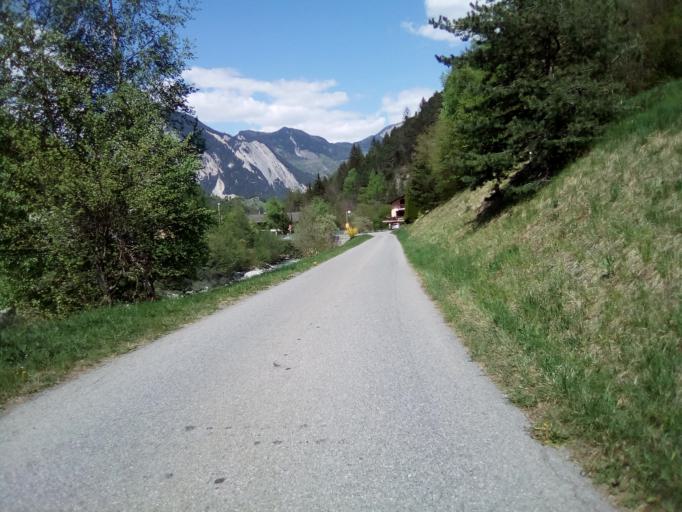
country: CH
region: Valais
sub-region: Entremont District
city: Orsieres
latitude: 46.0516
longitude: 7.1500
